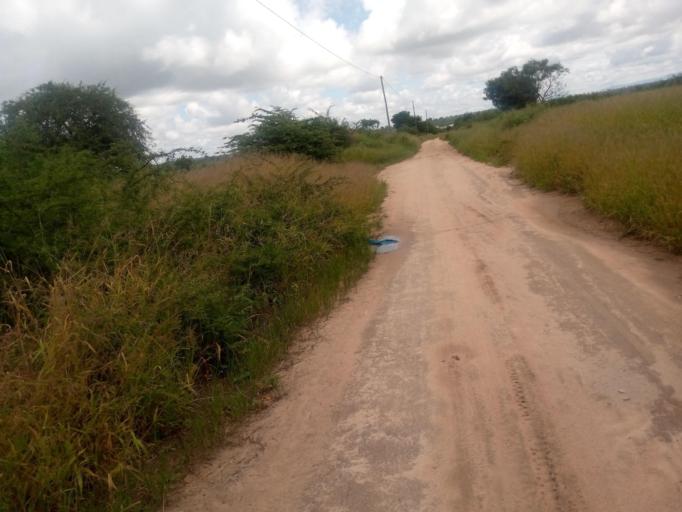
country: TZ
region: Dodoma
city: Dodoma
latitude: -6.1155
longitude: 35.7394
